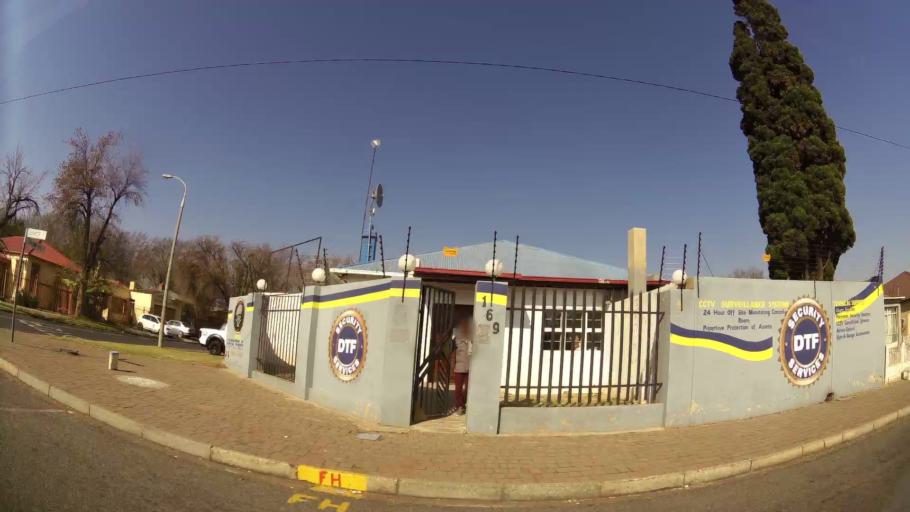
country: ZA
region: Gauteng
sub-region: Ekurhuleni Metropolitan Municipality
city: Boksburg
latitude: -26.2245
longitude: 28.2609
